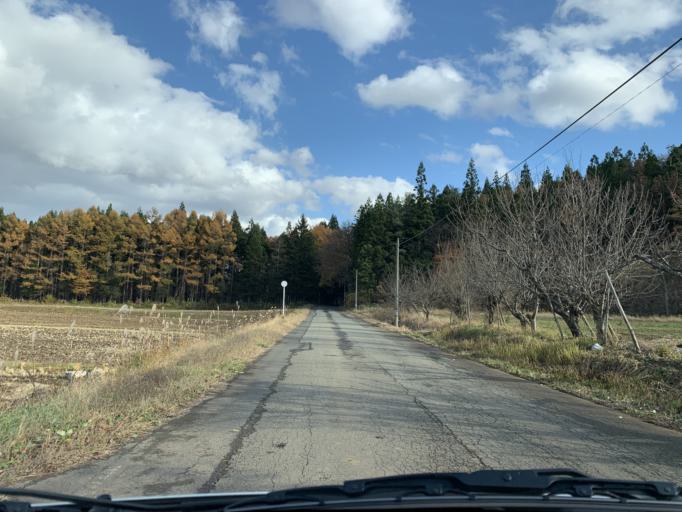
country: JP
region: Iwate
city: Mizusawa
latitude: 39.1053
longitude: 140.9745
